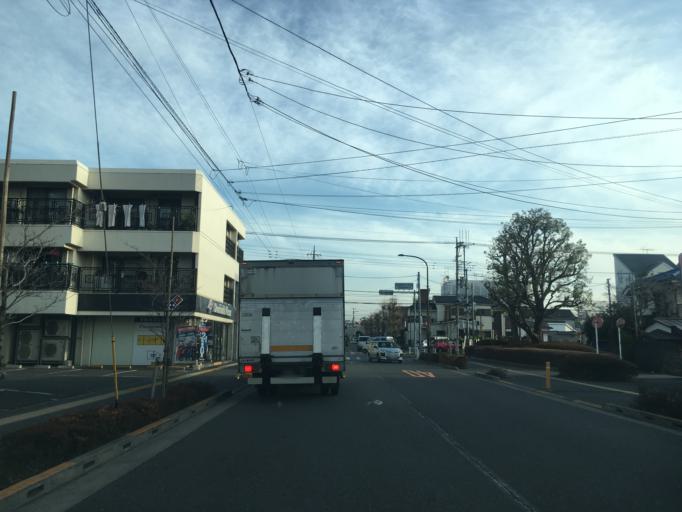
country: JP
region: Tokyo
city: Hino
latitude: 35.6902
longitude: 139.4235
